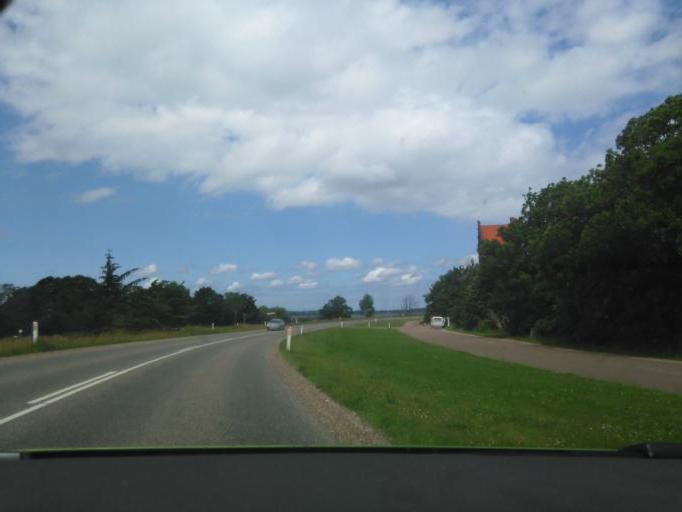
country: DK
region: Zealand
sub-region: Kalundborg Kommune
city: Hong
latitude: 55.5540
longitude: 11.3080
